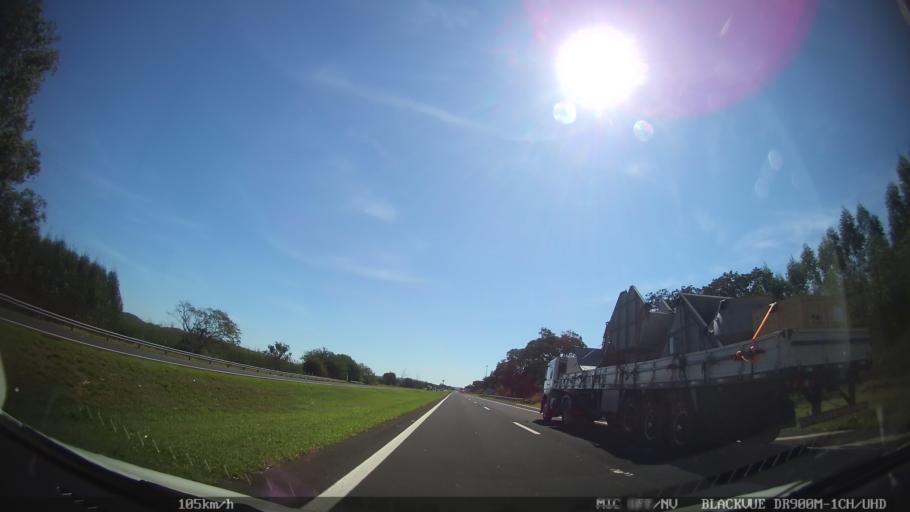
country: BR
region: Sao Paulo
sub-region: Sao Simao
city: Sao Simao
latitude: -21.5614
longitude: -47.6345
